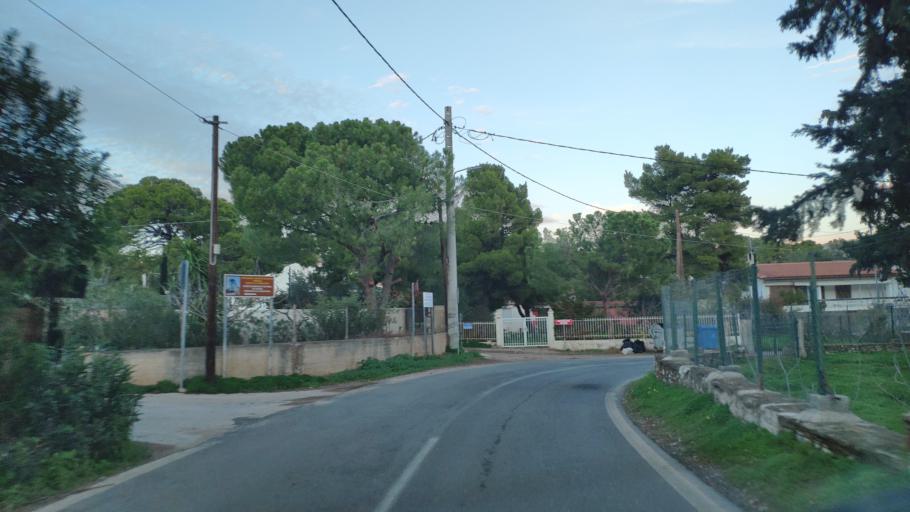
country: GR
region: Attica
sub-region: Nomarchia Anatolikis Attikis
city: Lavrio
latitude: 37.6657
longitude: 24.0359
